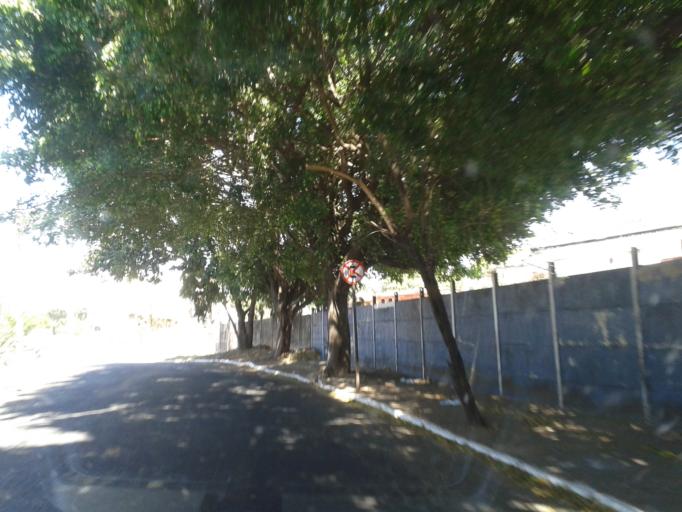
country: BR
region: Minas Gerais
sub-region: Araguari
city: Araguari
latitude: -18.6425
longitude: -48.1968
